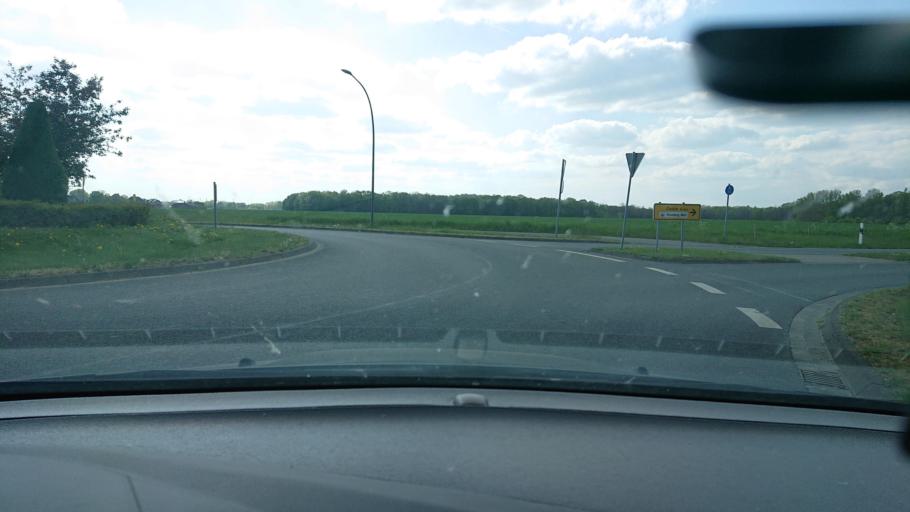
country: DE
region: North Rhine-Westphalia
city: Oelde
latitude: 51.8000
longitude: 8.1855
